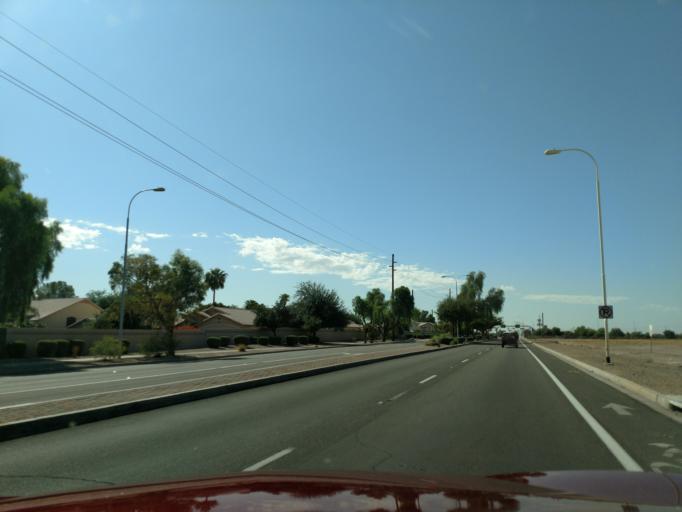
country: US
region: Arizona
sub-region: Maricopa County
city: Guadalupe
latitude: 33.2964
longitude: -111.9458
